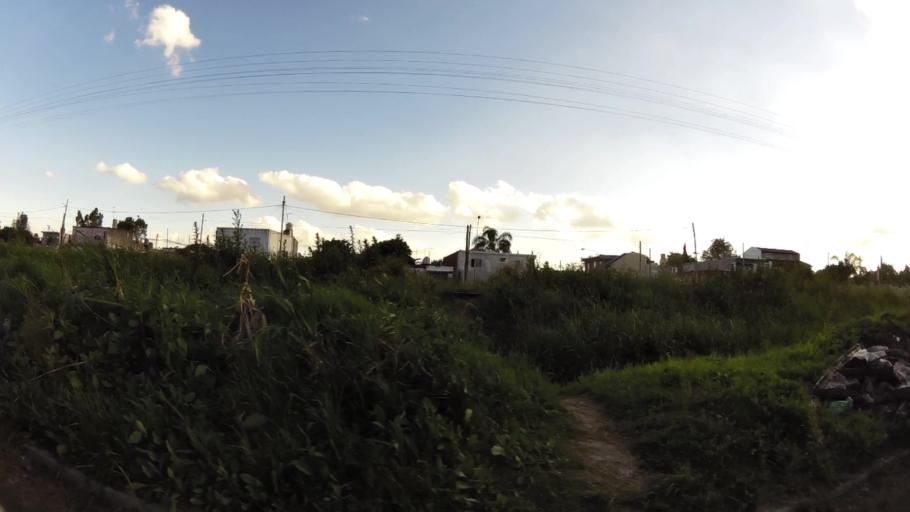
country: AR
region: Buenos Aires
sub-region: Partido de Moron
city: Moron
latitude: -34.6987
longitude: -58.6327
